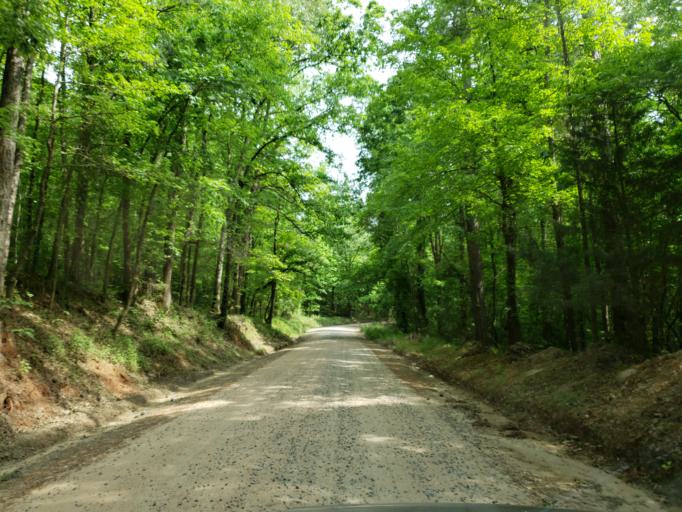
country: US
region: Georgia
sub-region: Monroe County
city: Forsyth
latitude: 32.9851
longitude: -83.9147
